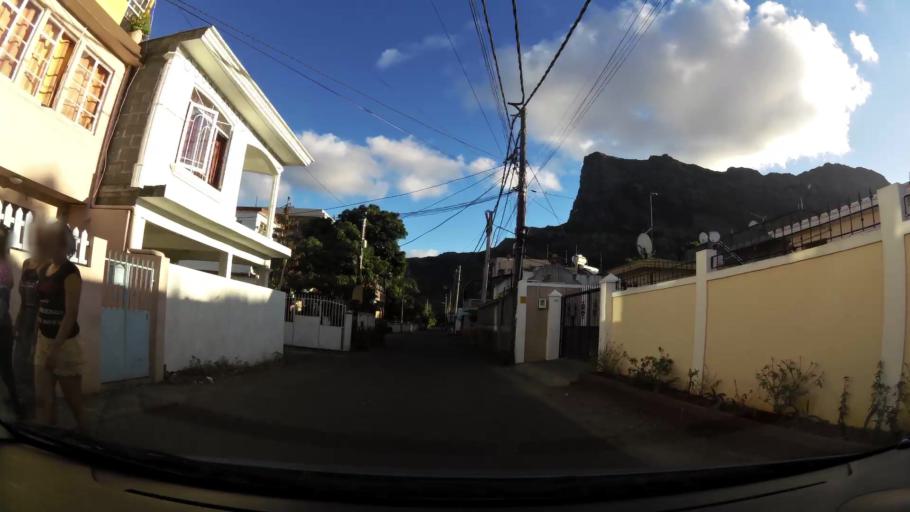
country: MU
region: Plaines Wilhems
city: Quatre Bornes
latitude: -20.2613
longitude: 57.4645
